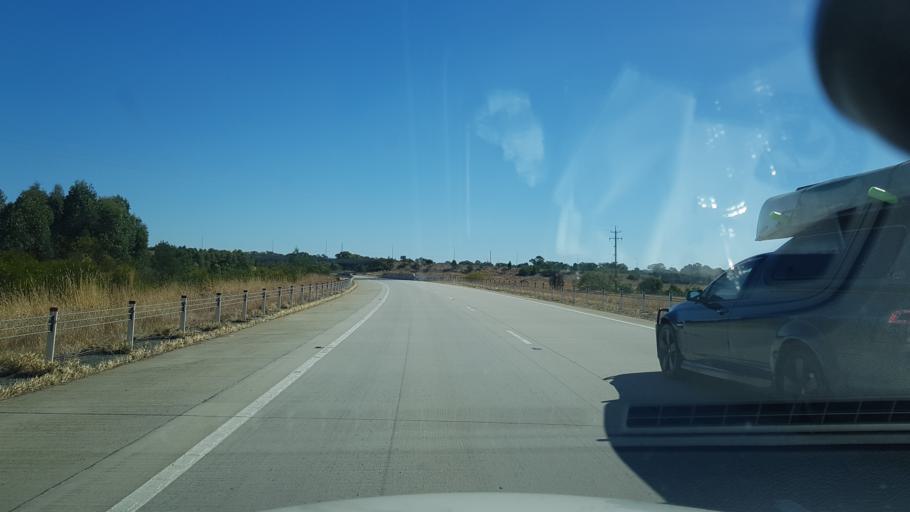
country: AU
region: New South Wales
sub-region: Greater Hume Shire
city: Jindera
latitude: -35.9252
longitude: 147.0121
